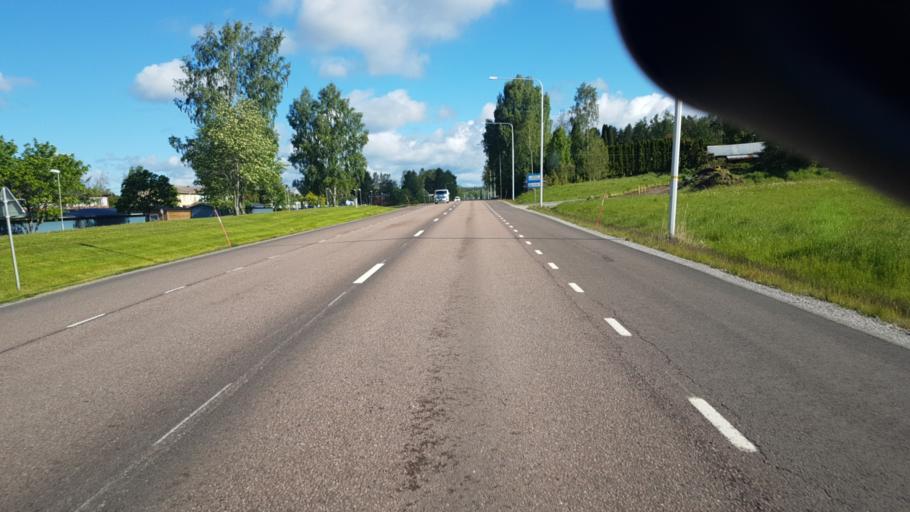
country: SE
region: Vaermland
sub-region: Arvika Kommun
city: Arvika
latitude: 59.6395
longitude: 12.6165
